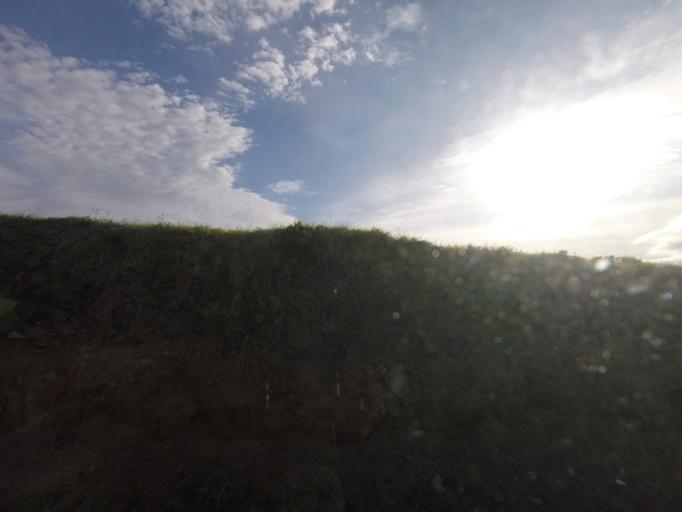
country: PT
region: Madeira
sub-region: Machico
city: Canical
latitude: 32.7480
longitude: -16.7404
